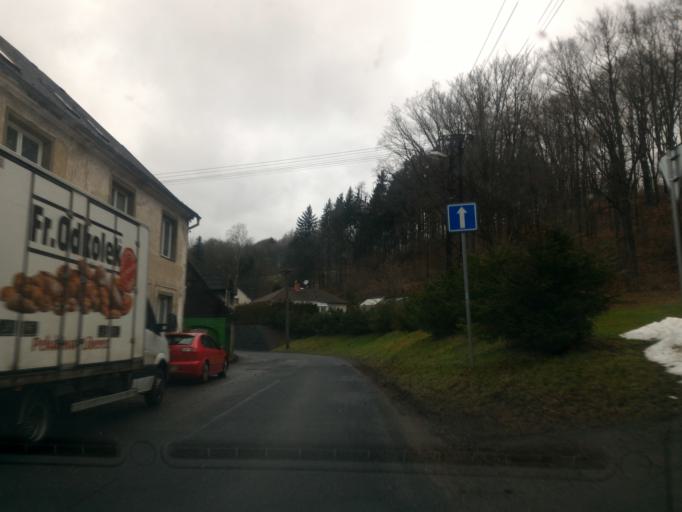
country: CZ
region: Ustecky
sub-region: Okres Decin
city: Krasna Lipa
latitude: 50.9150
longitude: 14.5027
